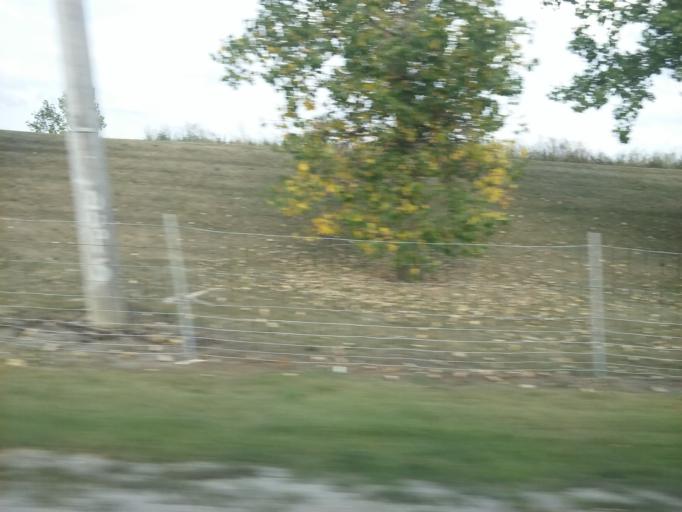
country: US
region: Ohio
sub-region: Wood County
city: Bowling Green
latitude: 41.3196
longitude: -83.6503
